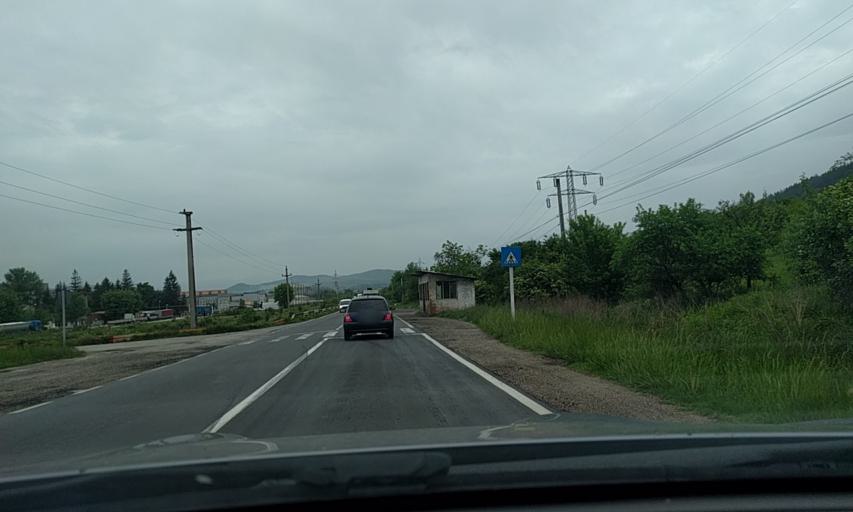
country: RO
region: Dambovita
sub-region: Comuna Vulcana-Pandele
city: Vulcana-Pandele
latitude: 45.0028
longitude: 25.4016
